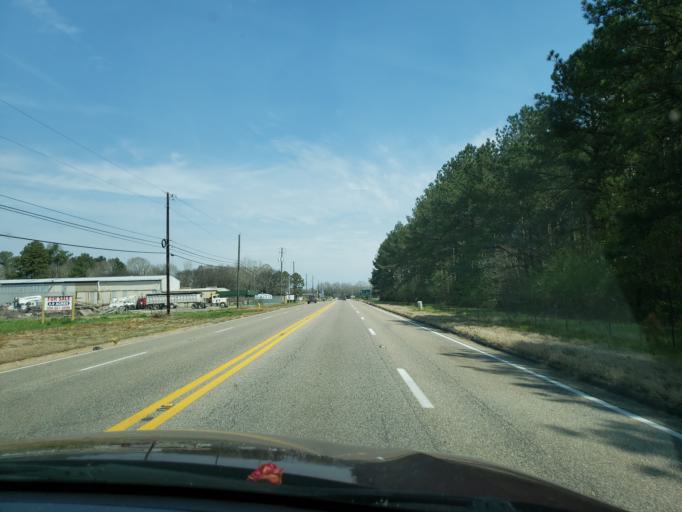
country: US
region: Alabama
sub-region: Elmore County
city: Wetumpka
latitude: 32.5364
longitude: -86.2303
